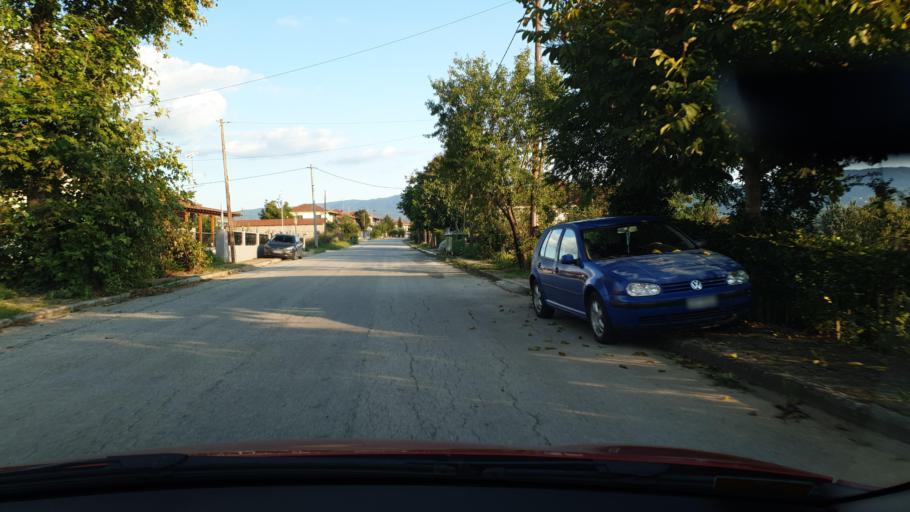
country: GR
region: Central Macedonia
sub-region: Nomos Thessalonikis
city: Nea Apollonia
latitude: 40.5489
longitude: 23.4463
